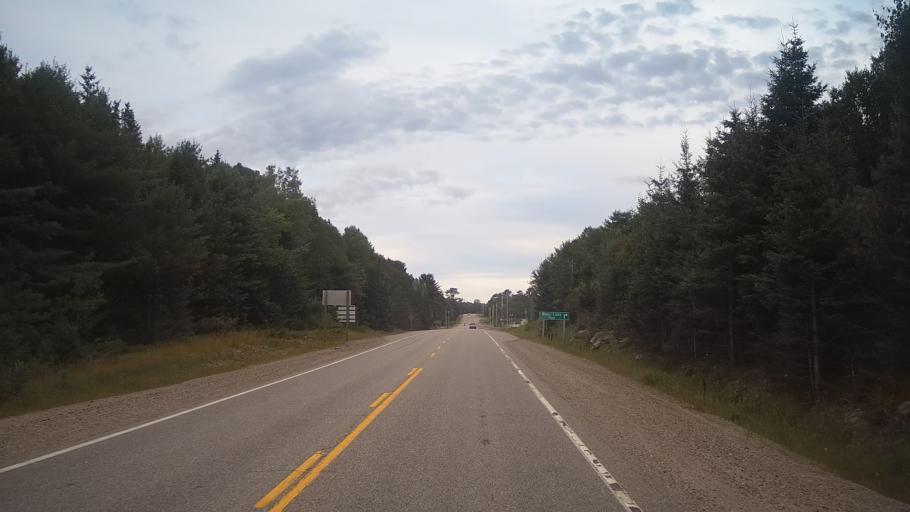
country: CA
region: Ontario
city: Deep River
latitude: 46.1367
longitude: -77.5575
